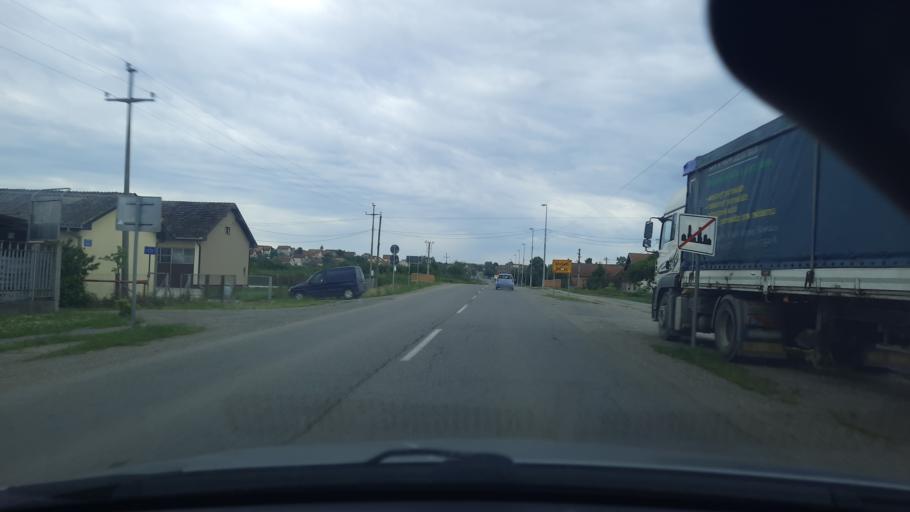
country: RS
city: Jevremovac
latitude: 44.7360
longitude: 19.6725
